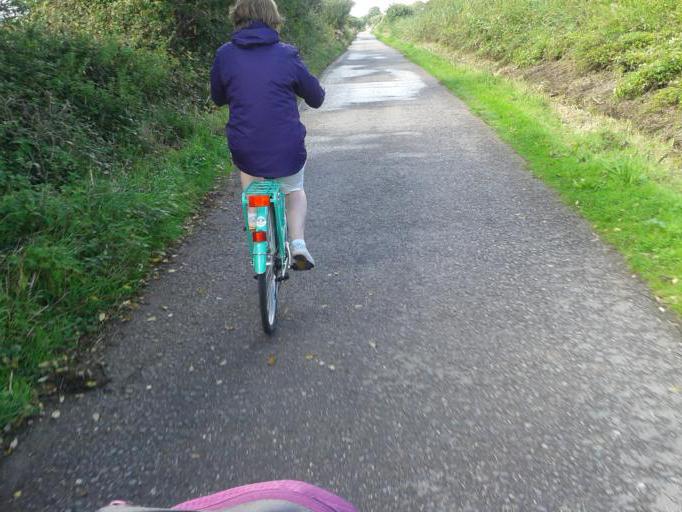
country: GB
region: England
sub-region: Devon
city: Topsham
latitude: 50.6677
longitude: -3.4688
